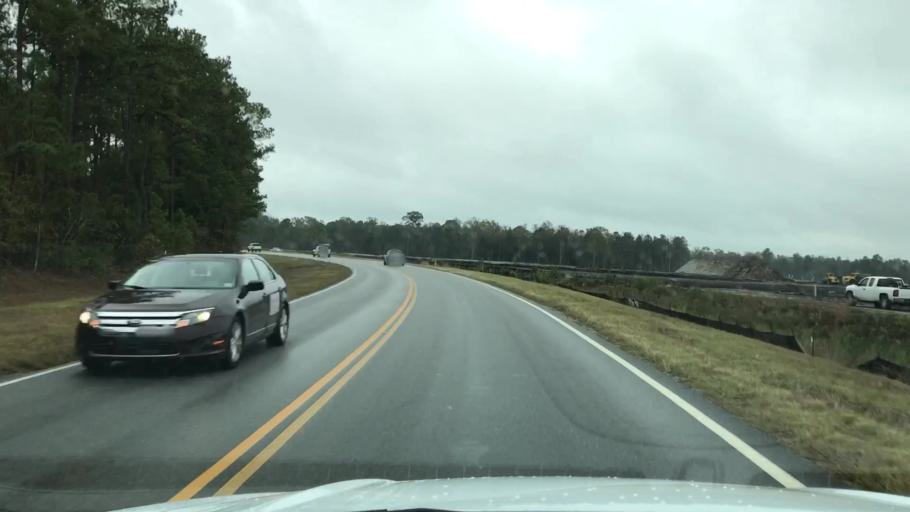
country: US
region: South Carolina
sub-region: Horry County
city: Myrtle Beach
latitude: 33.7553
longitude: -78.8824
